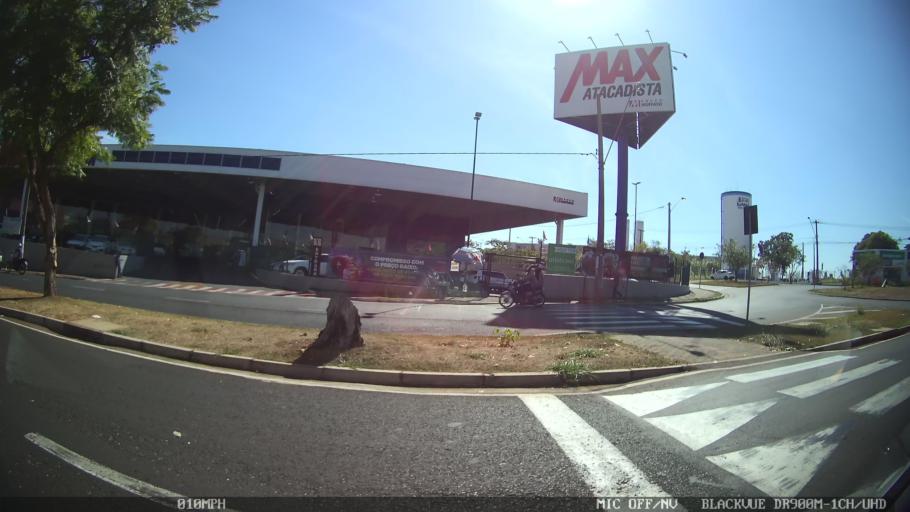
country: BR
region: Sao Paulo
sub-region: Sao Jose Do Rio Preto
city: Sao Jose do Rio Preto
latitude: -20.7811
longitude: -49.3779
